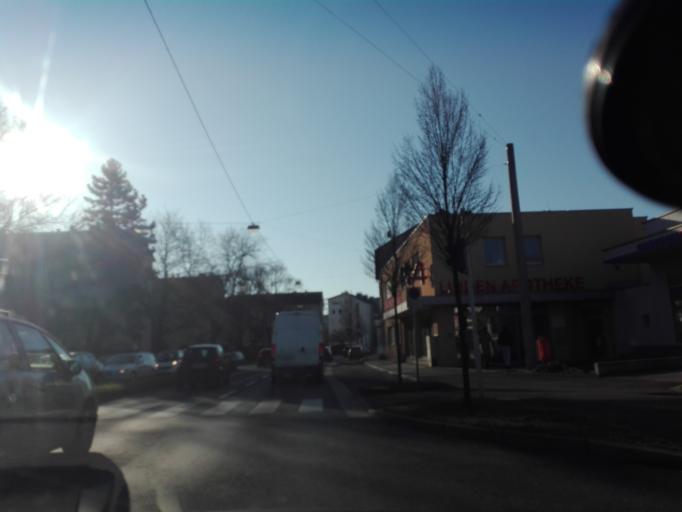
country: AT
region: Upper Austria
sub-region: Linz Stadt
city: Linz
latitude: 48.2797
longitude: 14.2811
